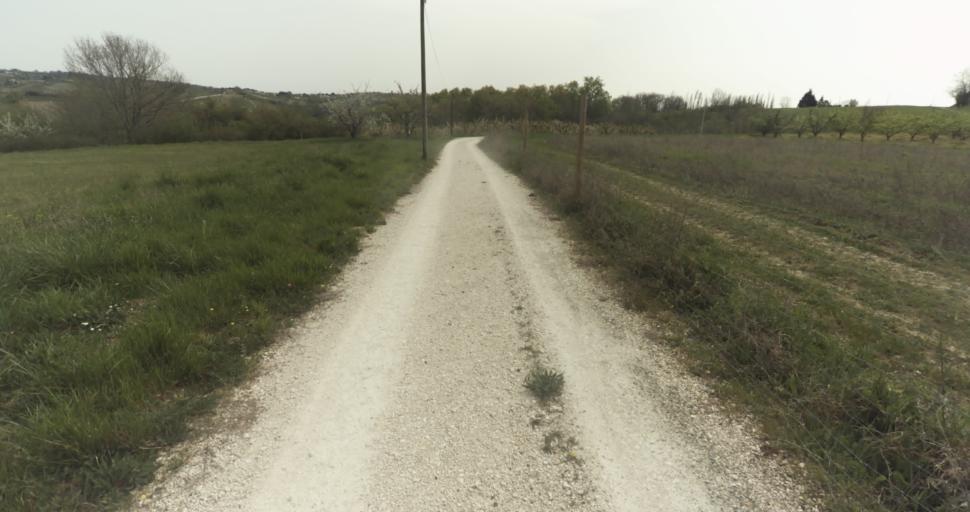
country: FR
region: Midi-Pyrenees
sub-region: Departement du Tarn-et-Garonne
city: Saint-Nicolas-de-la-Grave
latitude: 44.1103
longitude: 1.0439
